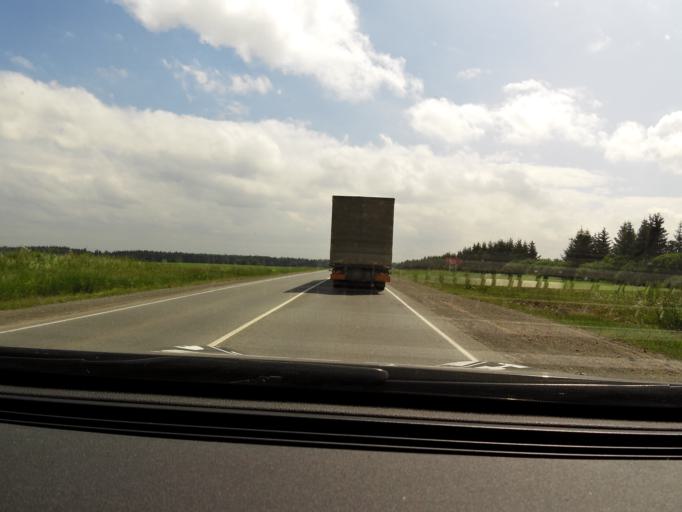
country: RU
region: Perm
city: Kukushtan
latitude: 57.5425
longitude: 56.5939
